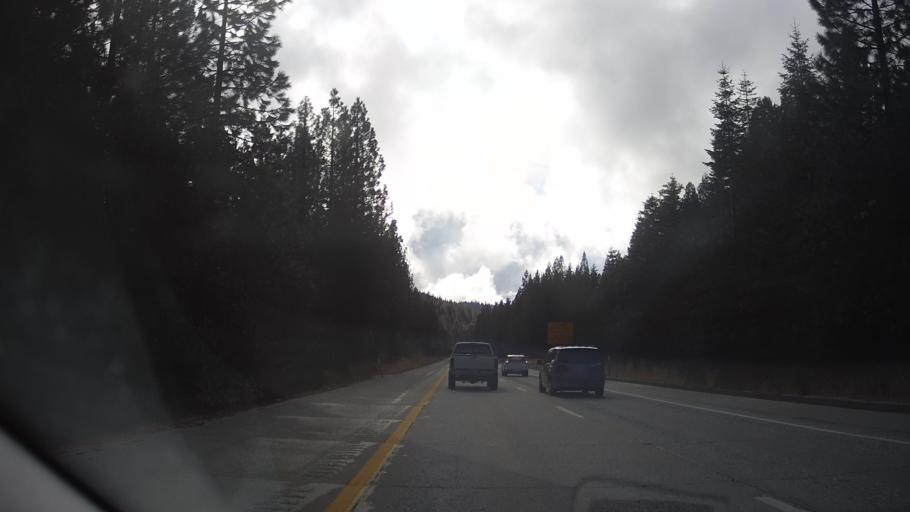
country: US
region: California
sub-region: Placer County
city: Foresthill
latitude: 39.2621
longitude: -120.7302
